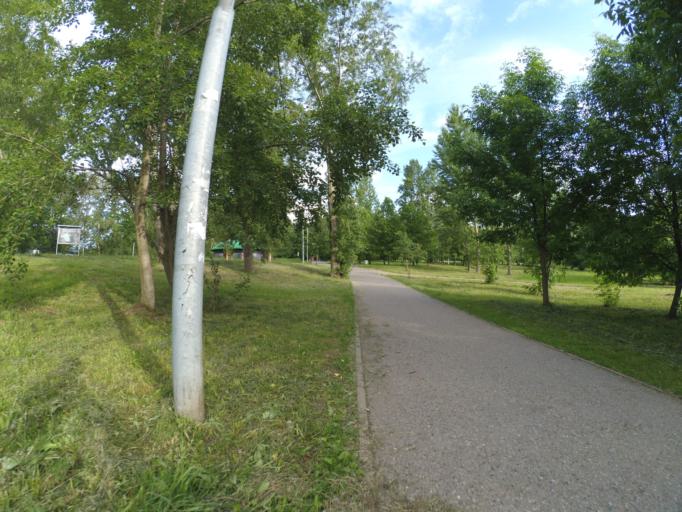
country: RU
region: Moscow
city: Ramenki
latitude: 55.6858
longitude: 37.4987
